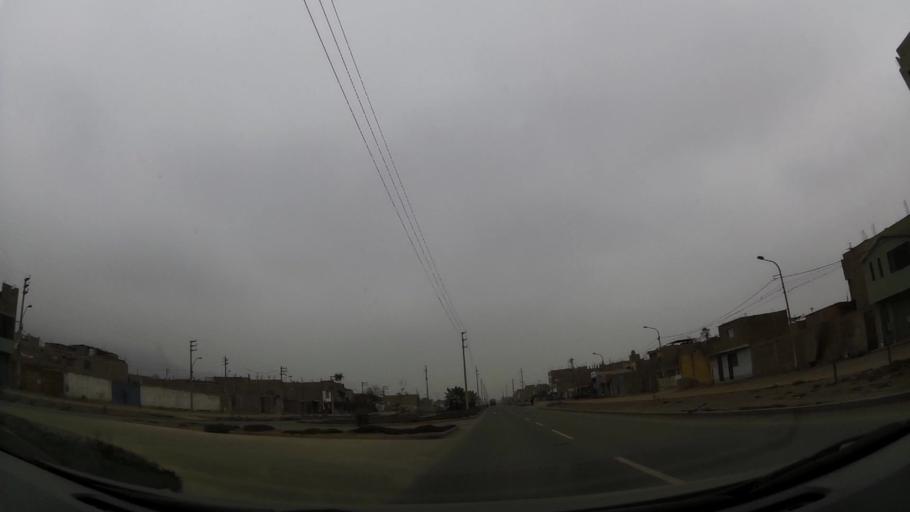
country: PE
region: Lima
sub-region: Lima
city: Urb. Santo Domingo
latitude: -11.8783
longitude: -77.0265
